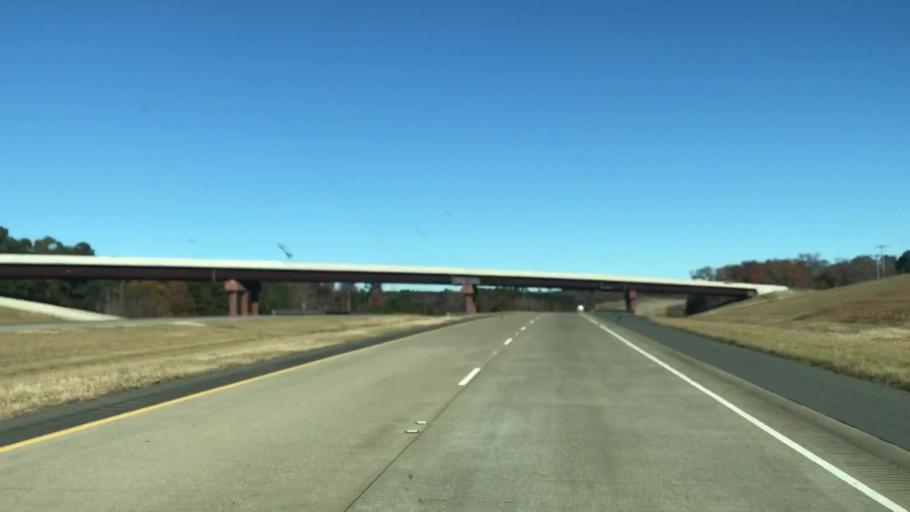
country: US
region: Louisiana
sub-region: Caddo Parish
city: Vivian
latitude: 32.9769
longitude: -93.9092
